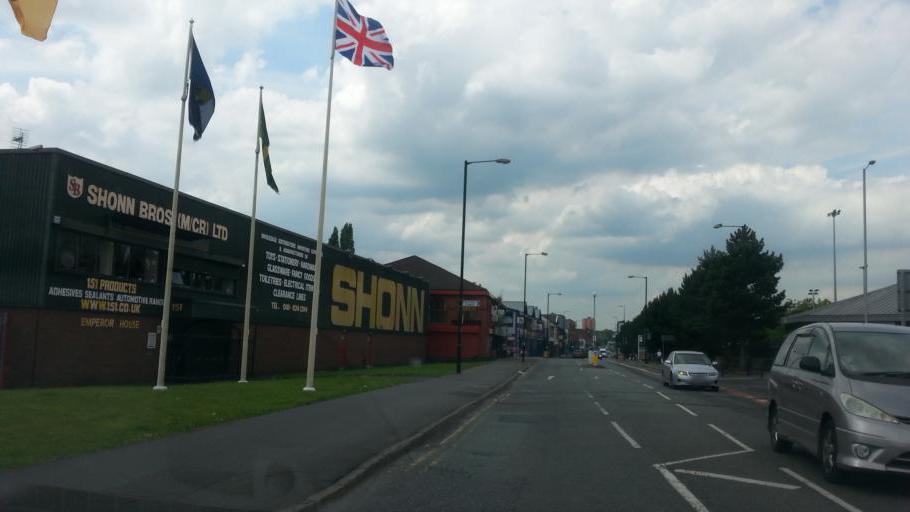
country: GB
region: England
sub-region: Manchester
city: Cheetham Hill
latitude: 53.4906
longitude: -2.2474
